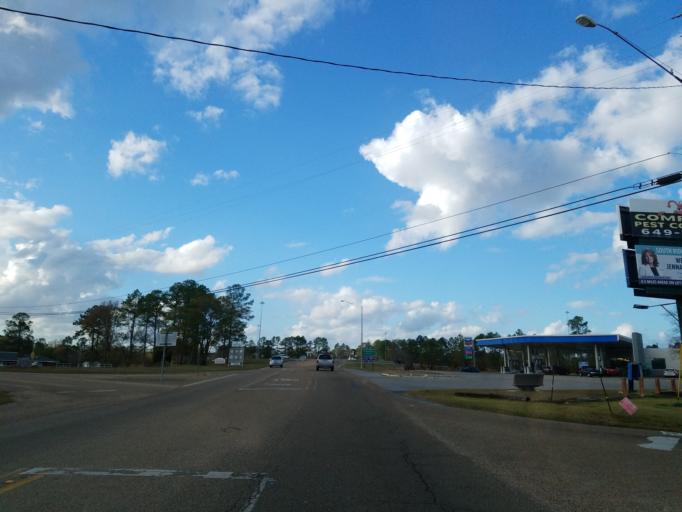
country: US
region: Mississippi
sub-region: Jones County
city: Ellisville
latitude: 31.6109
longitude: -89.2053
